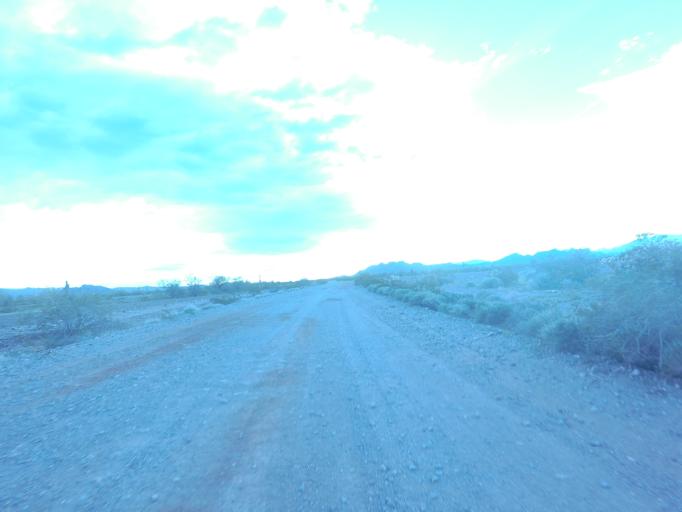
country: US
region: Arizona
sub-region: La Paz County
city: Quartzsite
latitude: 33.5341
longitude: -114.1986
